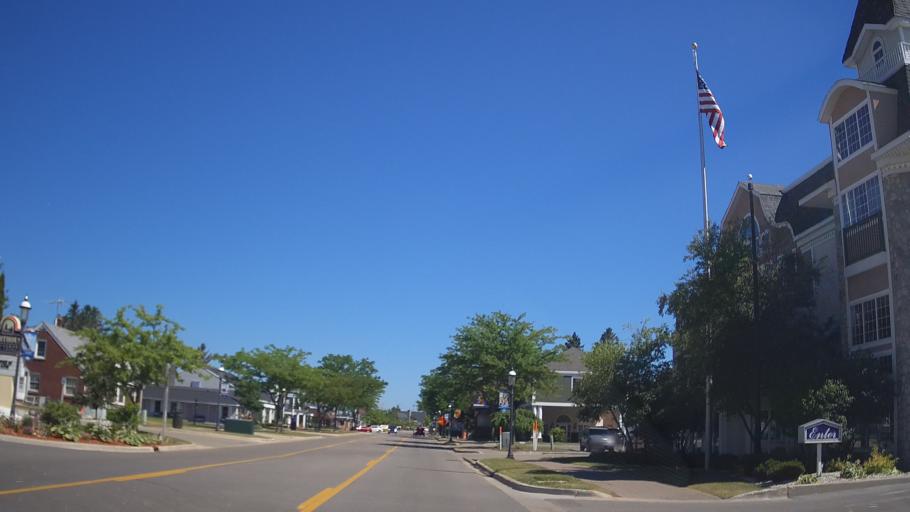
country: US
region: Michigan
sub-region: Mackinac County
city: Saint Ignace
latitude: 45.7748
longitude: -84.7267
